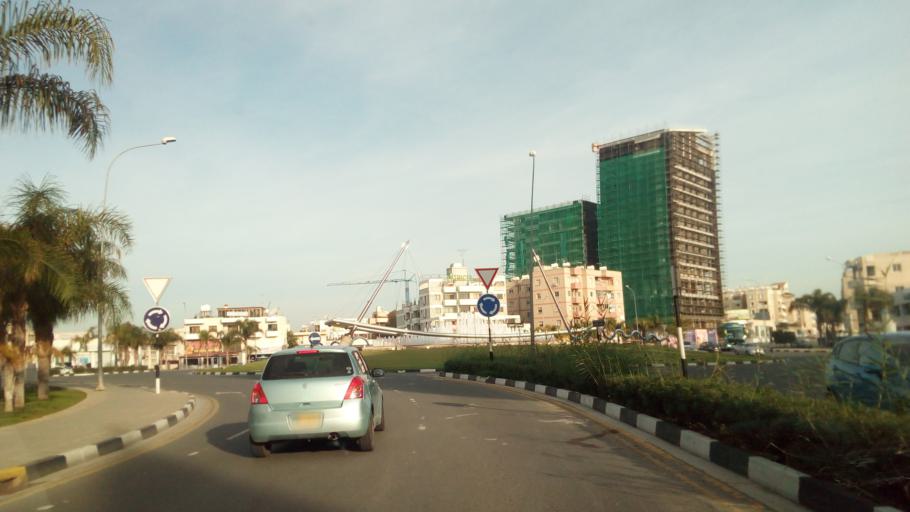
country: CY
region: Larnaka
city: Larnaca
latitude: 34.9296
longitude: 33.6372
